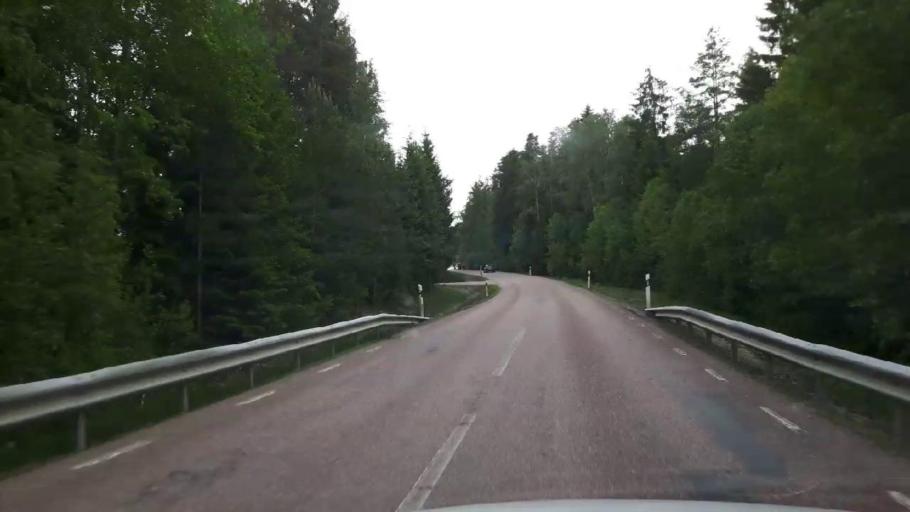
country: SE
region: Vaestmanland
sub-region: Skinnskattebergs Kommun
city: Skinnskatteberg
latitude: 59.8464
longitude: 15.8414
